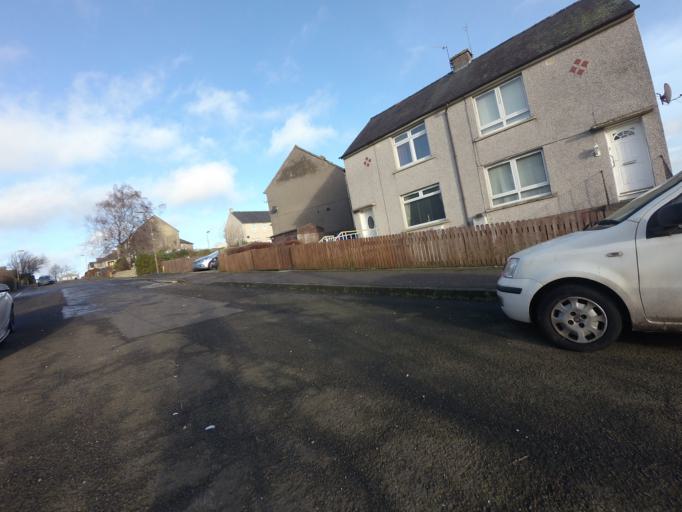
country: GB
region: Scotland
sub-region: West Lothian
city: West Calder
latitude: 55.8771
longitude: -3.5862
